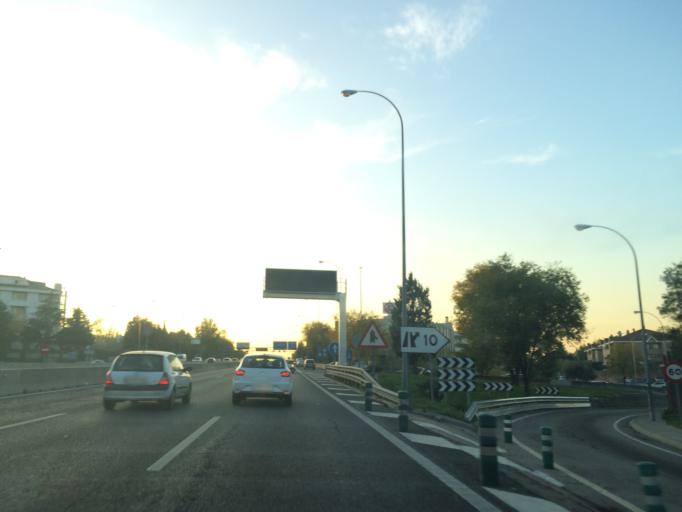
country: ES
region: Madrid
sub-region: Provincia de Madrid
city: Pozuelo de Alarcon
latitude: 40.4636
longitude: -3.7824
